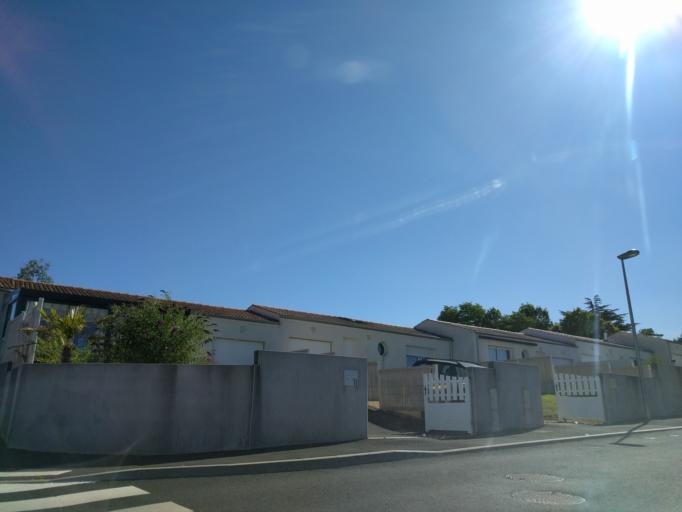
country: FR
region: Poitou-Charentes
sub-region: Departement des Deux-Sevres
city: Niort
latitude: 46.3405
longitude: -0.4480
